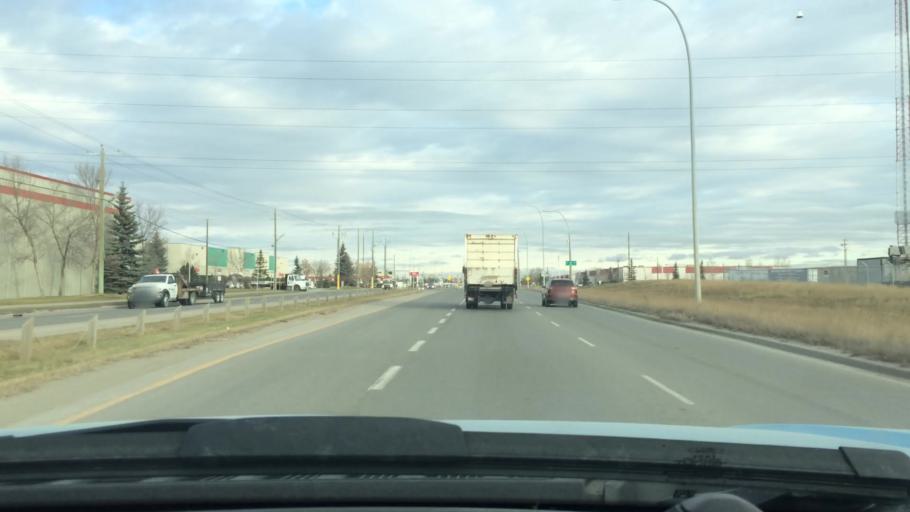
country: CA
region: Alberta
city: Calgary
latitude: 51.0057
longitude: -113.9585
